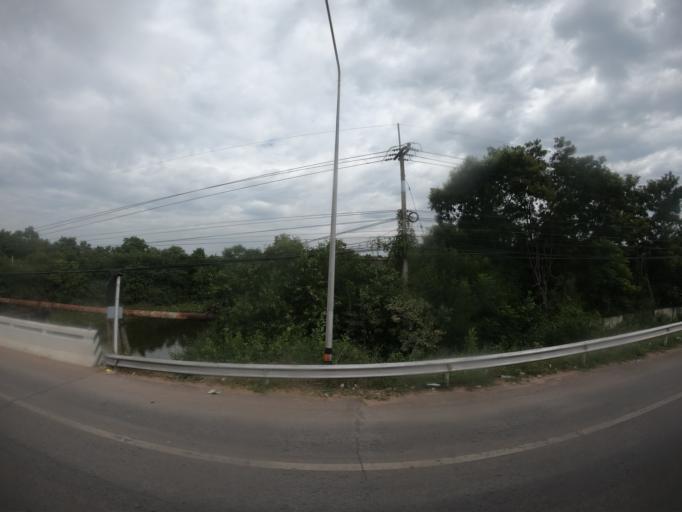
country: TH
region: Maha Sarakham
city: Maha Sarakham
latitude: 16.2046
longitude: 103.2872
